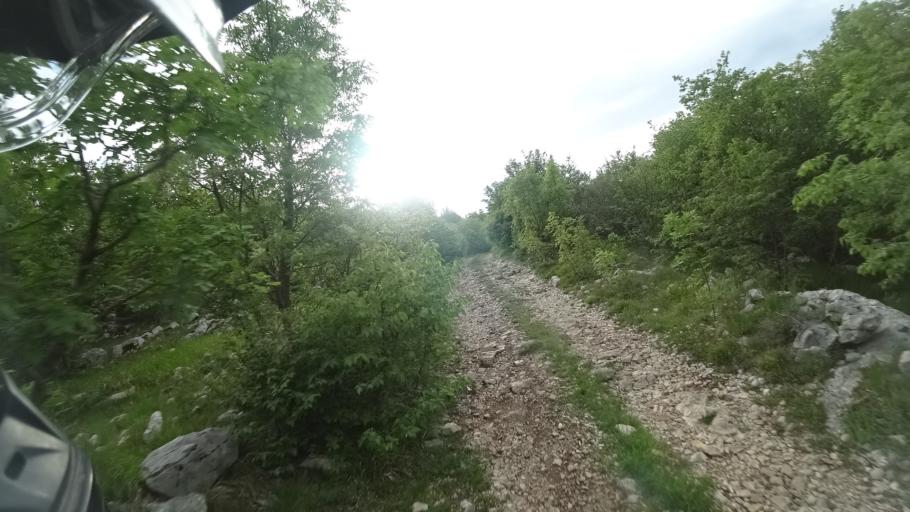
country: HR
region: Sibensko-Kniniska
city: Drnis
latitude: 43.8707
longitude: 16.3818
